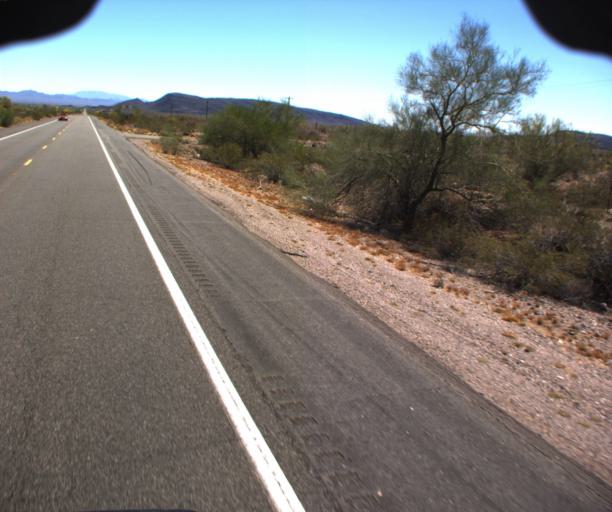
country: US
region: Arizona
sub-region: La Paz County
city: Quartzsite
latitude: 33.6657
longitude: -114.0016
